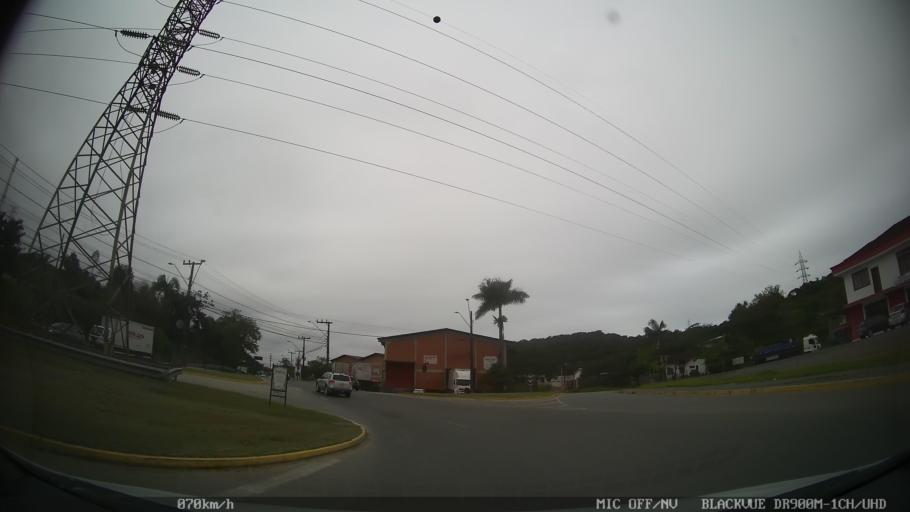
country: BR
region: Santa Catarina
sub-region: Joinville
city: Joinville
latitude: -26.2929
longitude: -48.8883
